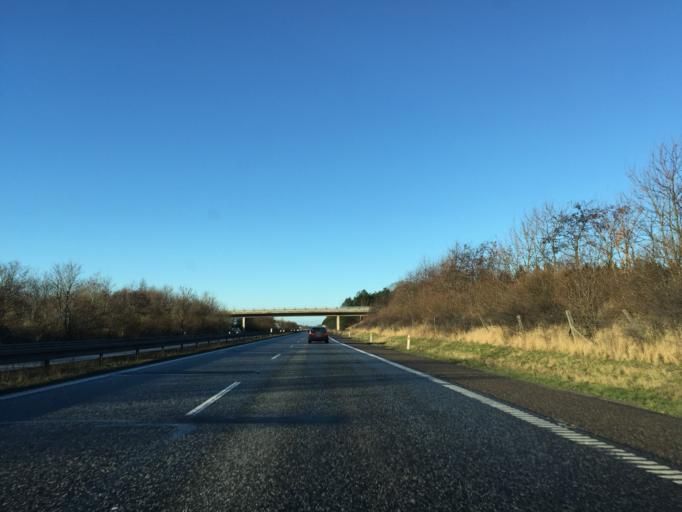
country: DK
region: South Denmark
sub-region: Kerteminde Kommune
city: Langeskov
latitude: 55.3576
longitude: 10.5556
